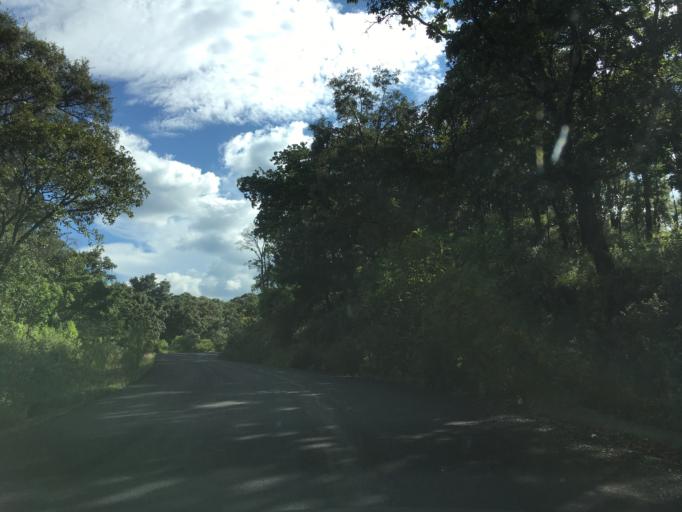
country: MX
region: Michoacan
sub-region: Zacapu
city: Naranja de Tapia
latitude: 19.7504
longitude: -101.7947
